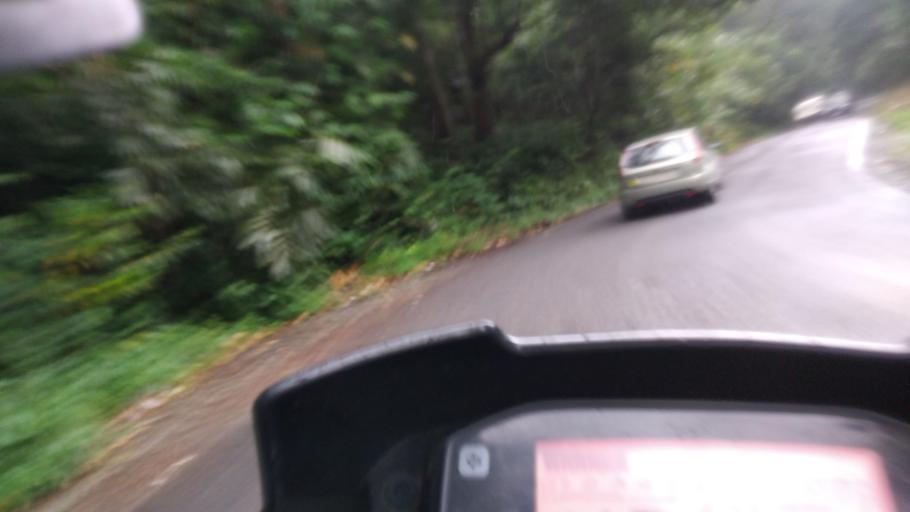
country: IN
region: Kerala
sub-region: Idukki
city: Kuttampuzha
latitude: 10.0639
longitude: 76.7988
